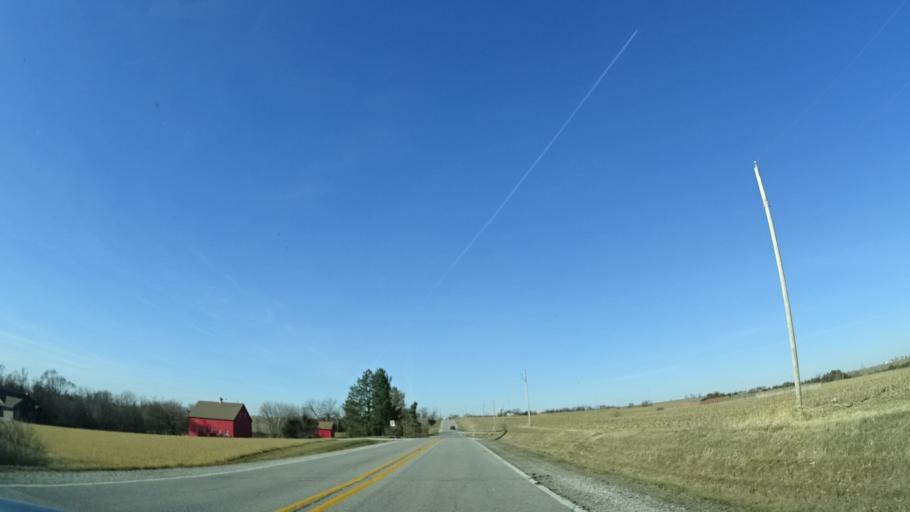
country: US
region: Nebraska
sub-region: Sarpy County
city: Papillion
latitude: 41.0890
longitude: -96.0591
